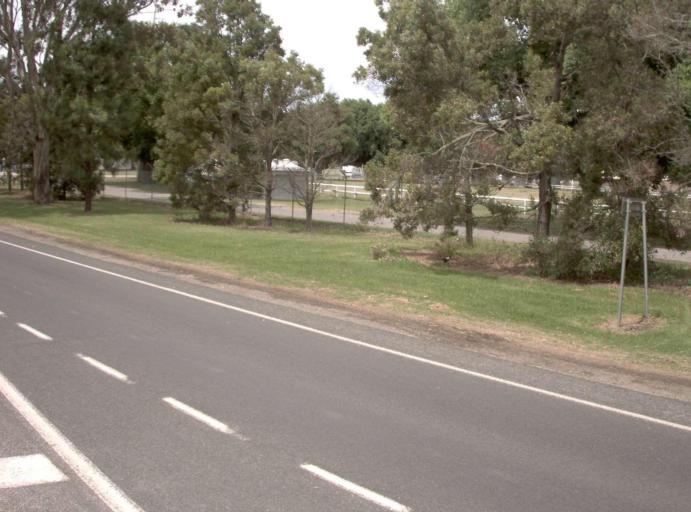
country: AU
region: Victoria
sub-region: Wellington
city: Sale
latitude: -38.0913
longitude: 147.0658
